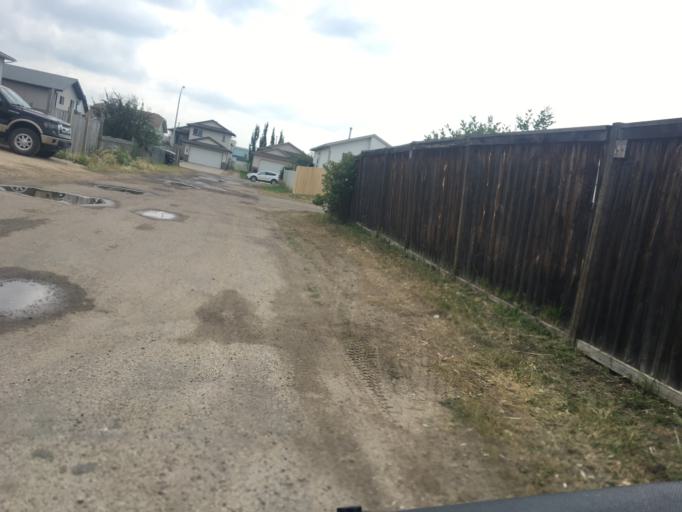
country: CA
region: Alberta
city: Grande Prairie
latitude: 55.1460
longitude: -118.8151
